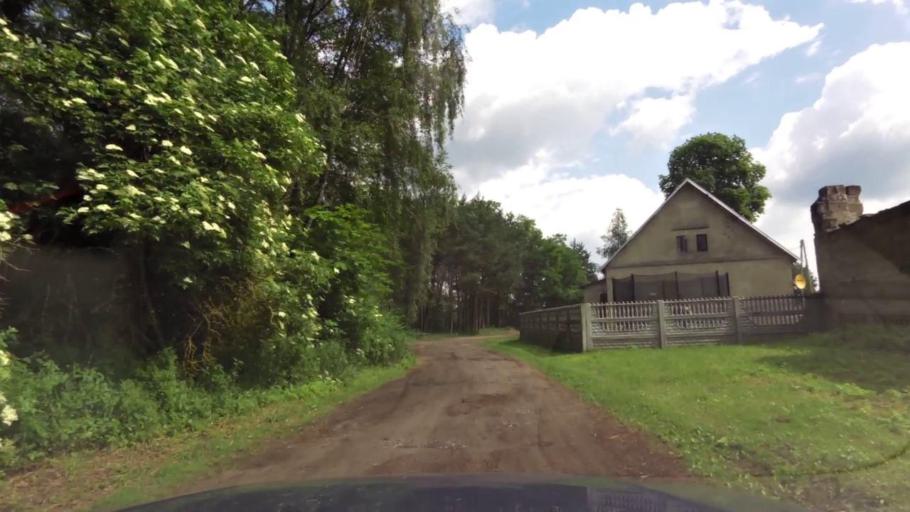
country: PL
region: West Pomeranian Voivodeship
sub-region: Powiat pyrzycki
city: Lipiany
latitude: 52.9645
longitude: 14.9234
